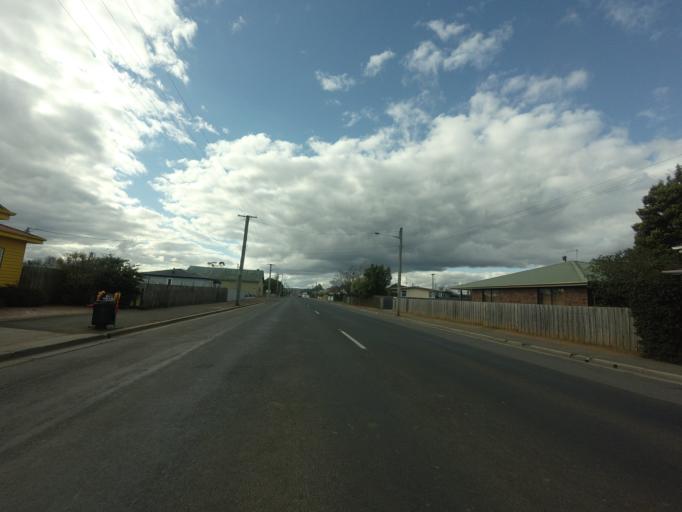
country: AU
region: Tasmania
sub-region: Northern Midlands
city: Longford
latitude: -41.6026
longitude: 147.1195
